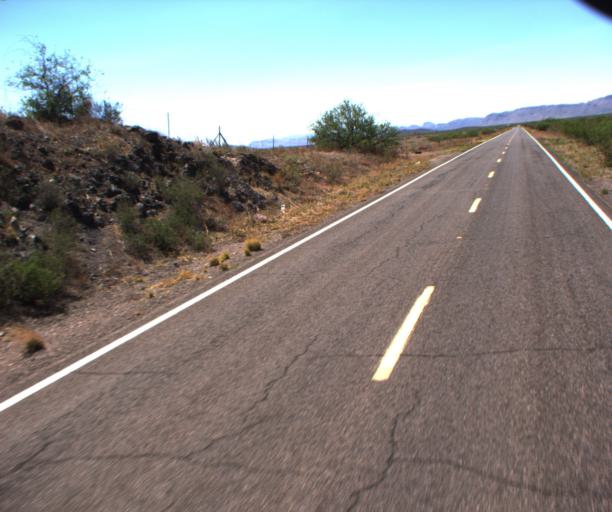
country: US
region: Arizona
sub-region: Cochise County
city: Douglas
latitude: 31.5361
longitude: -109.2909
